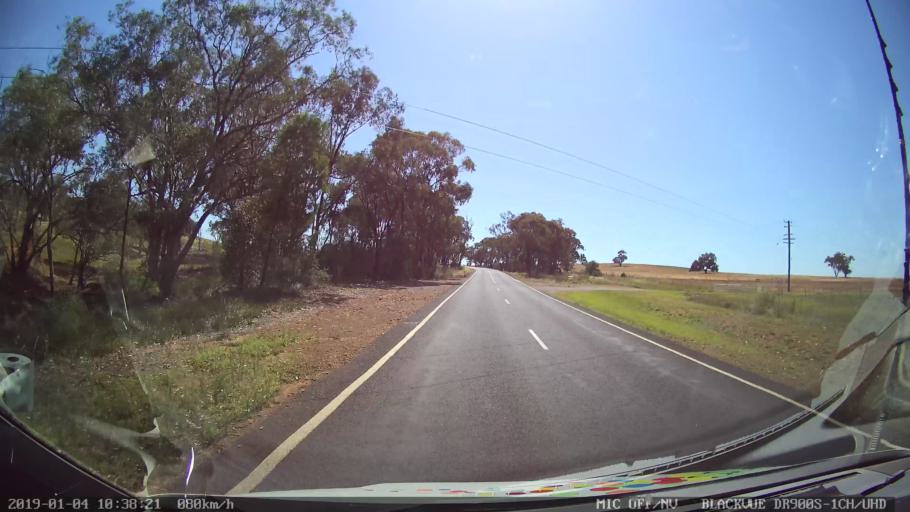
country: AU
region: New South Wales
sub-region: Cabonne
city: Molong
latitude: -33.2930
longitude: 148.7074
